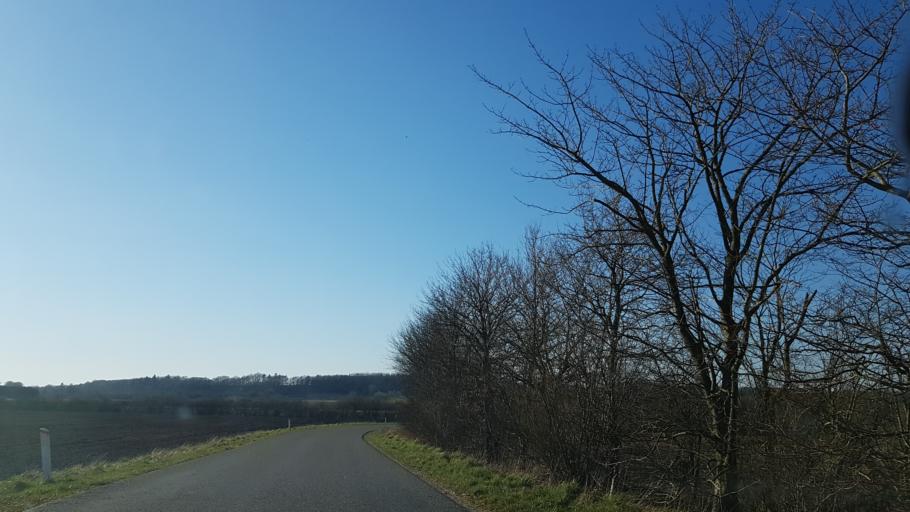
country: DK
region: South Denmark
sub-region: Vejen Kommune
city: Brorup
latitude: 55.4259
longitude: 8.9565
